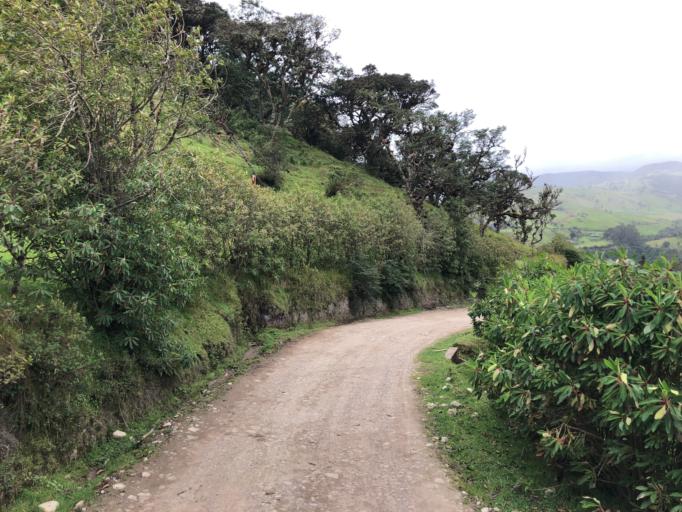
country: CO
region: Cauca
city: Totoro
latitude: 2.4727
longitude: -76.3449
